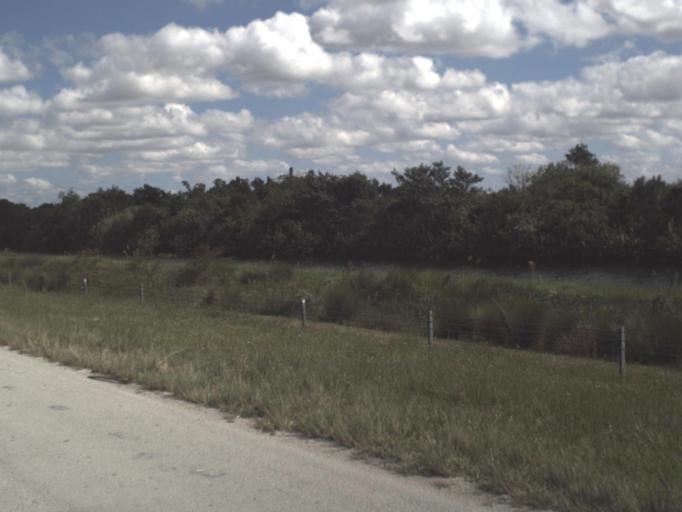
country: US
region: Florida
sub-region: Miami-Dade County
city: Palm Springs North
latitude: 25.9314
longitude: -80.3722
